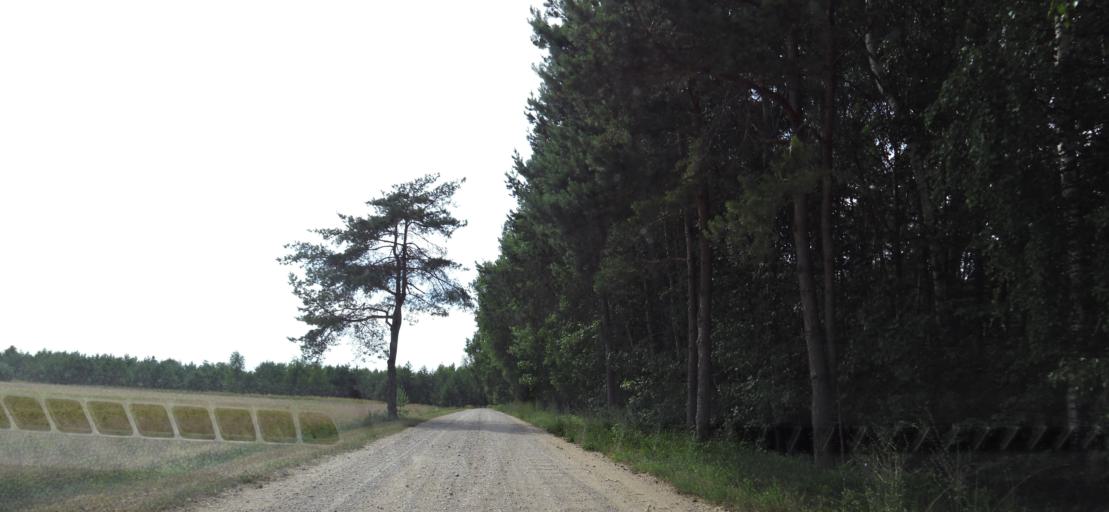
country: LT
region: Panevezys
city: Pasvalys
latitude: 55.9663
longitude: 24.3084
